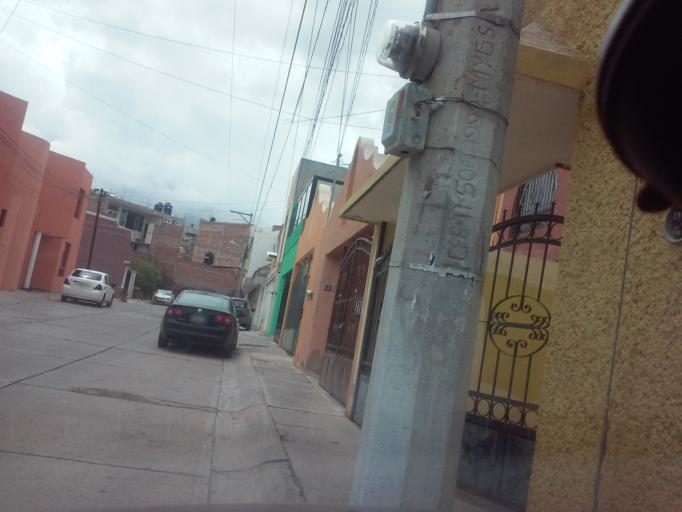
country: MX
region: Zacatecas
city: Guadalupe
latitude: 22.7511
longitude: -102.5268
